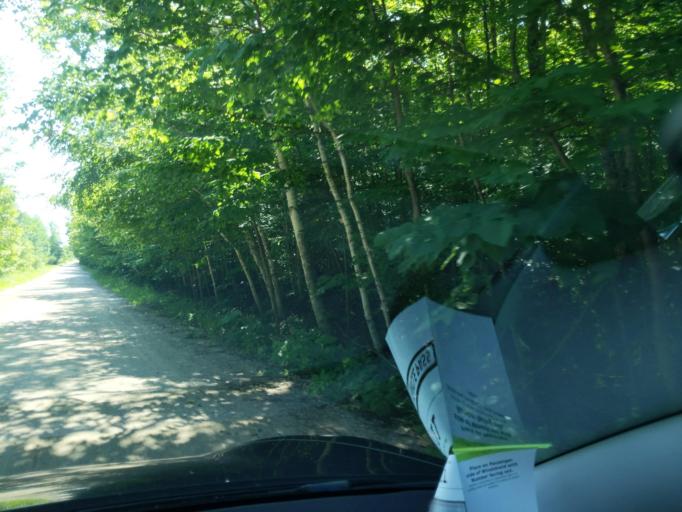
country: US
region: Michigan
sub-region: Mackinac County
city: Saint Ignace
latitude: 45.6792
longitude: -84.6693
